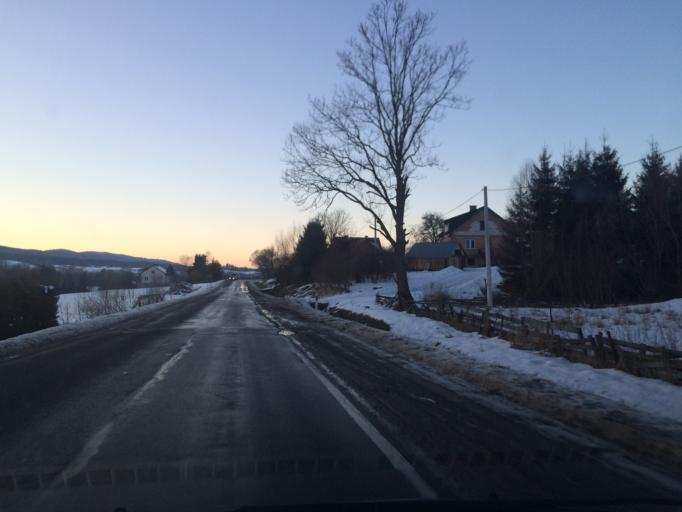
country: PL
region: Subcarpathian Voivodeship
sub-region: Powiat bieszczadzki
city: Czarna
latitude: 49.3674
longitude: 22.6586
